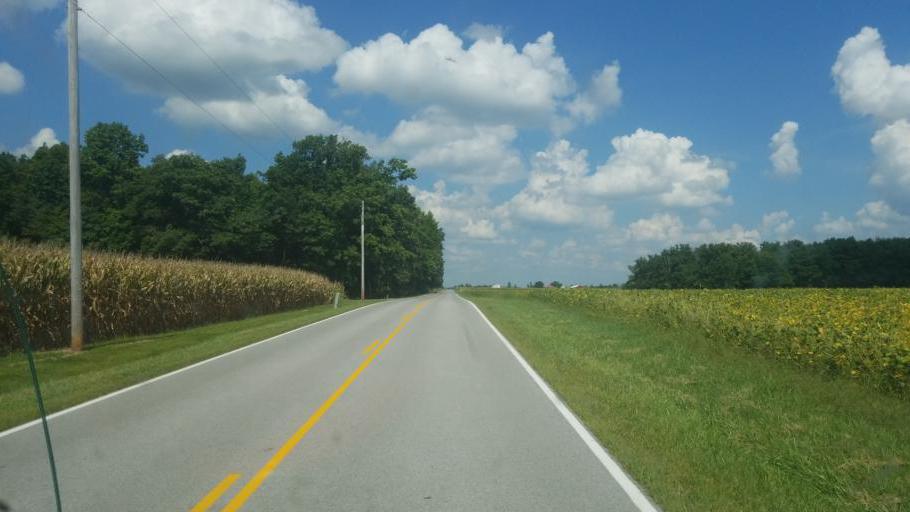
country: US
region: Ohio
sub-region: Hancock County
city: Arlington
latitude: 40.8659
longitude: -83.7274
